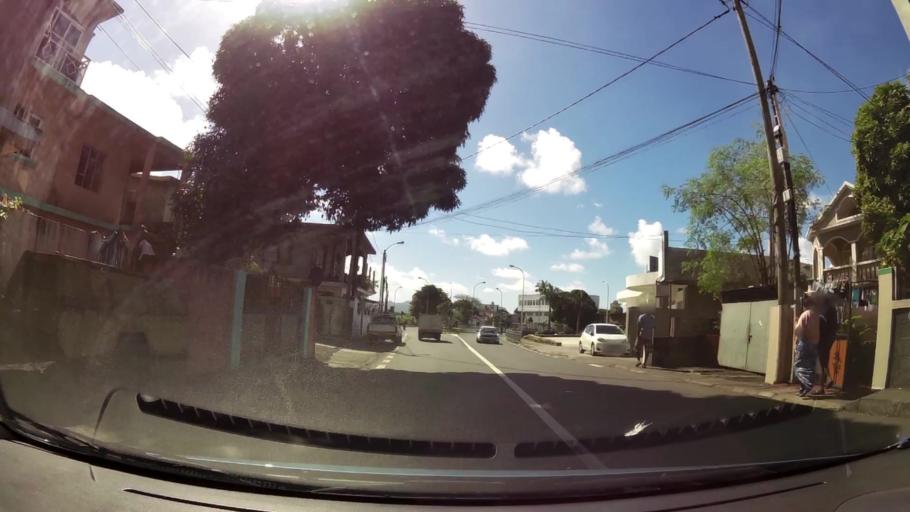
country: MU
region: Grand Port
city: Plaine Magnien
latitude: -20.4303
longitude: 57.6658
